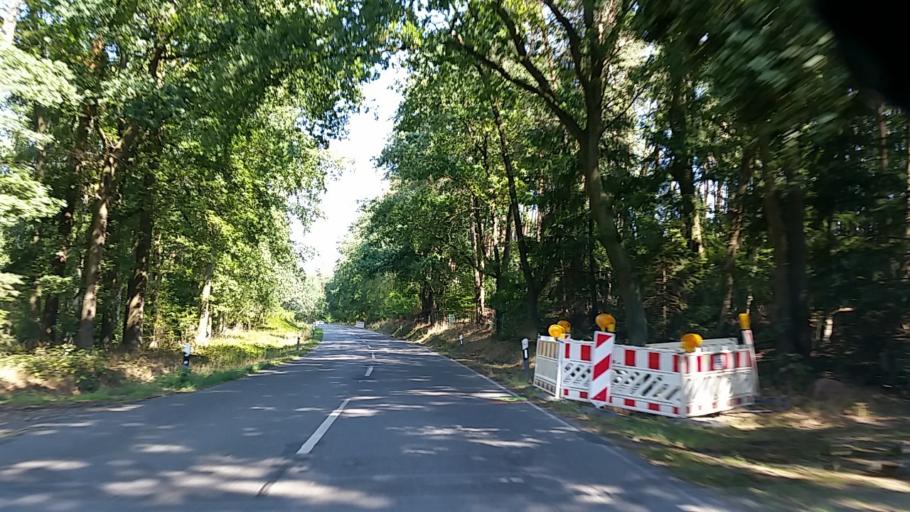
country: DE
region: Lower Saxony
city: Jelmstorf
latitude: 53.1110
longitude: 10.5470
